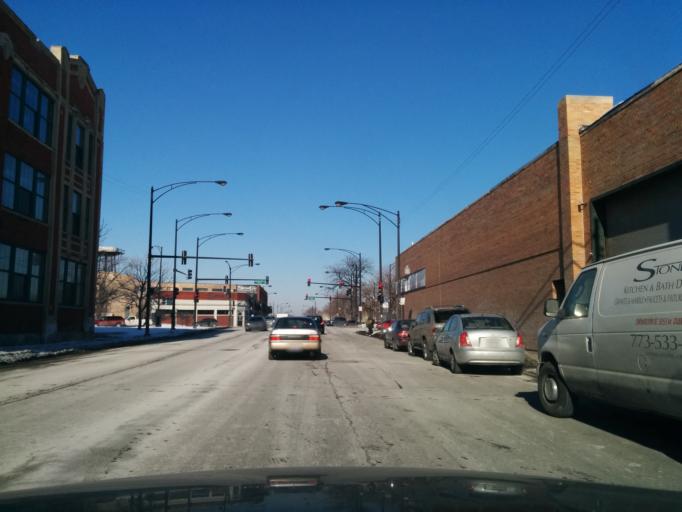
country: US
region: Illinois
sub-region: Cook County
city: Chicago
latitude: 41.8962
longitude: -87.7011
